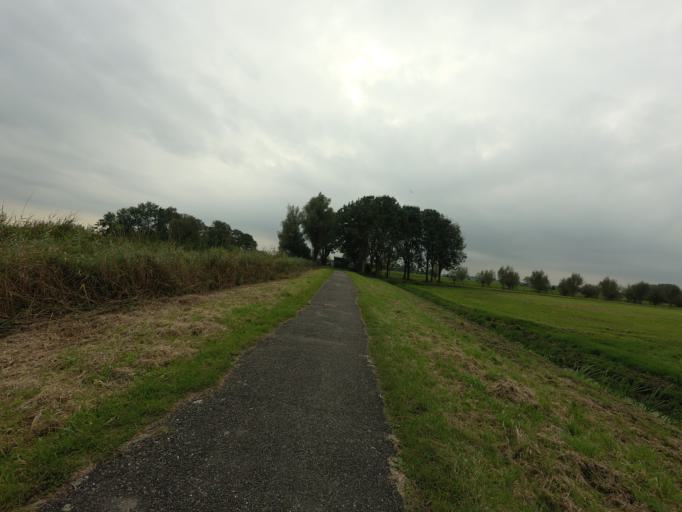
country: NL
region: South Holland
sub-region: Molenwaard
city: Liesveld
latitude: 51.8934
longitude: 4.7770
